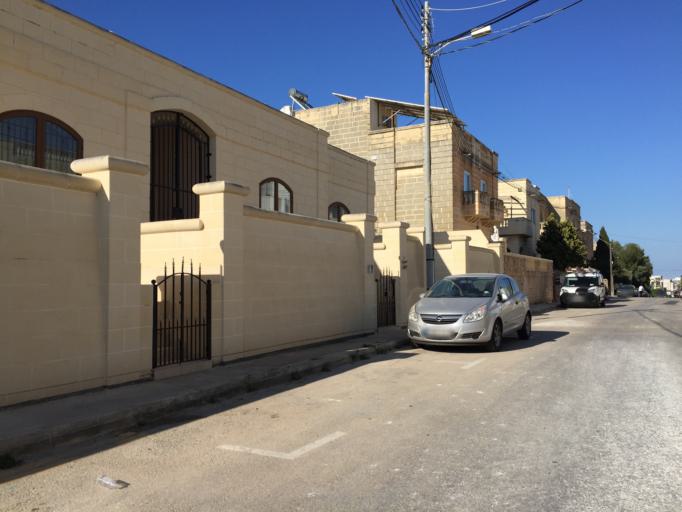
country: MT
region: Saint John
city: Saint John
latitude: 35.9055
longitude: 14.4813
